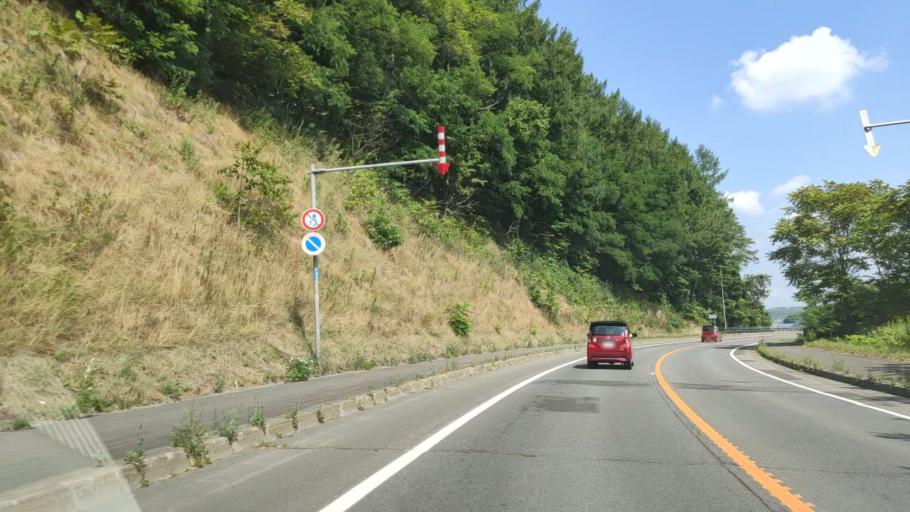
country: JP
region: Hokkaido
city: Shimo-furano
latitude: 43.4715
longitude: 142.4530
